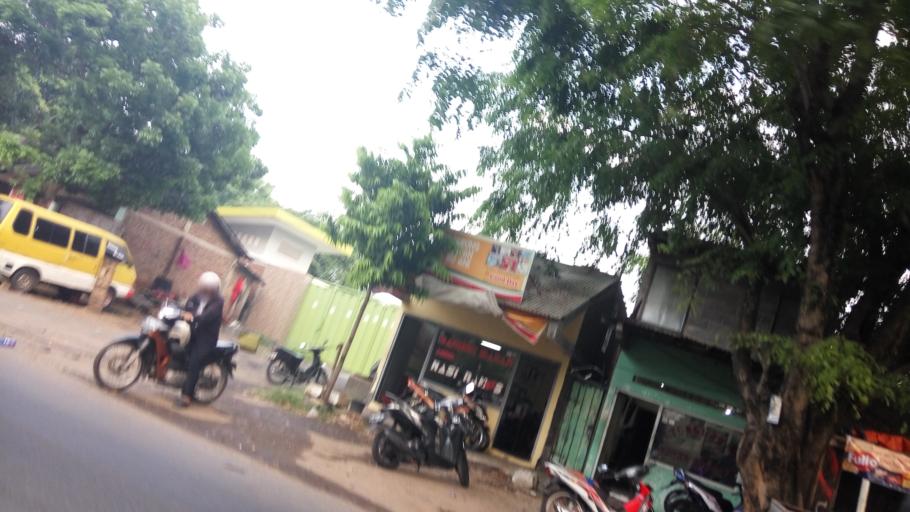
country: ID
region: Central Java
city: Semarang
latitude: -7.0035
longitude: 110.3919
